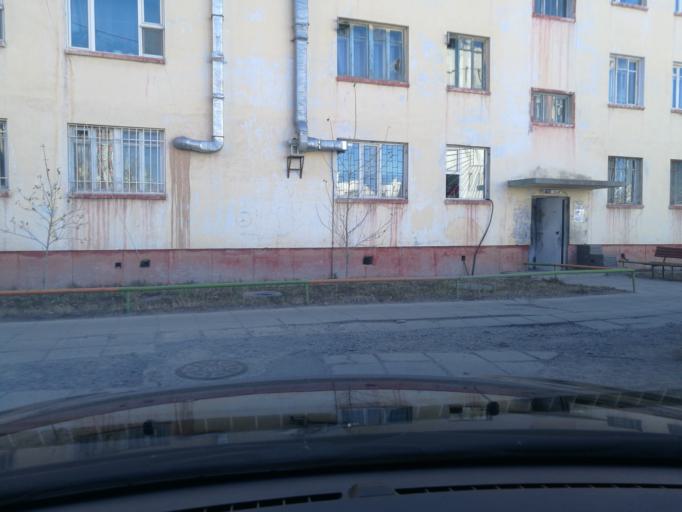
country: MN
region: Ulaanbaatar
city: Ulaanbaatar
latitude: 47.9019
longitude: 106.9089
